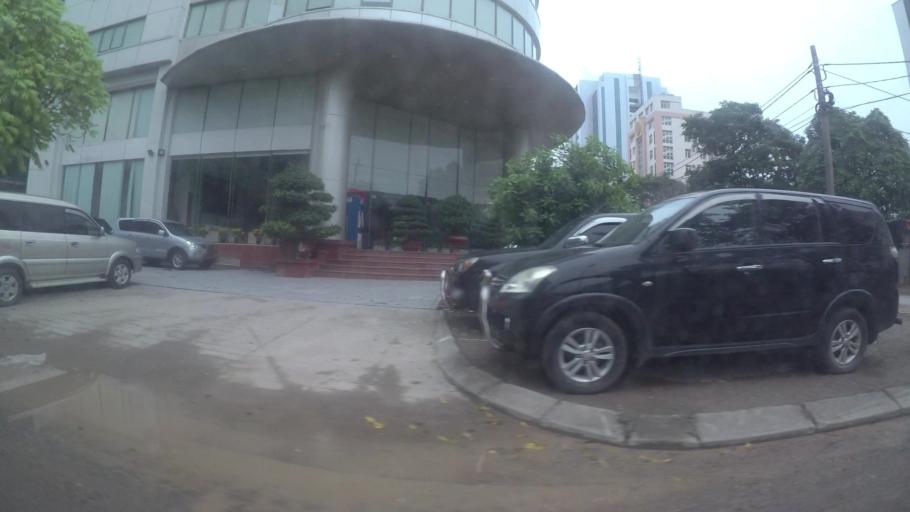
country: VN
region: Ha Noi
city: Cau Dien
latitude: 21.0302
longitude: 105.7818
